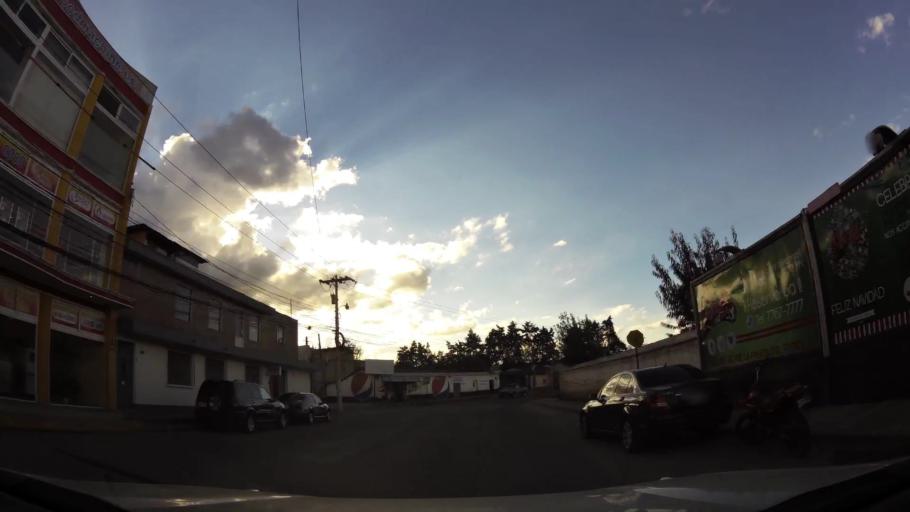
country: GT
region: Quetzaltenango
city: Quetzaltenango
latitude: 14.8500
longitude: -91.5291
